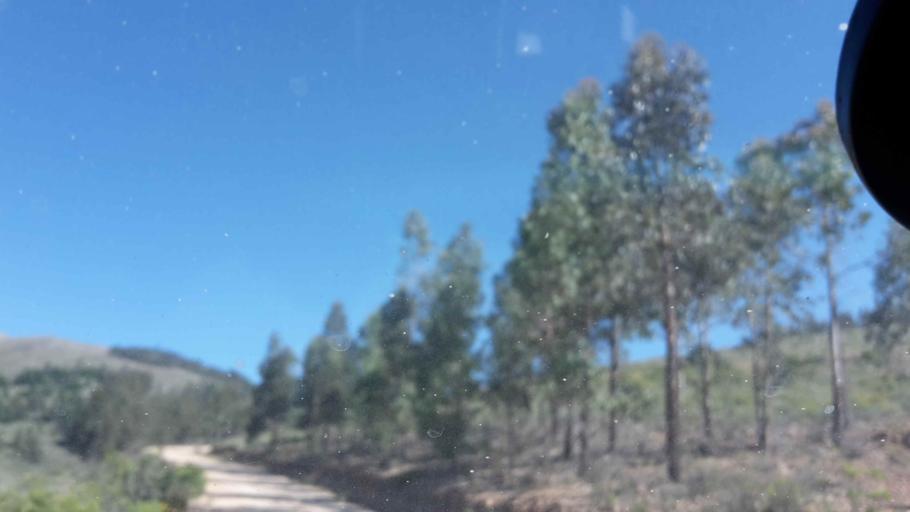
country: BO
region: Cochabamba
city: Arani
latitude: -17.6622
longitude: -65.7338
